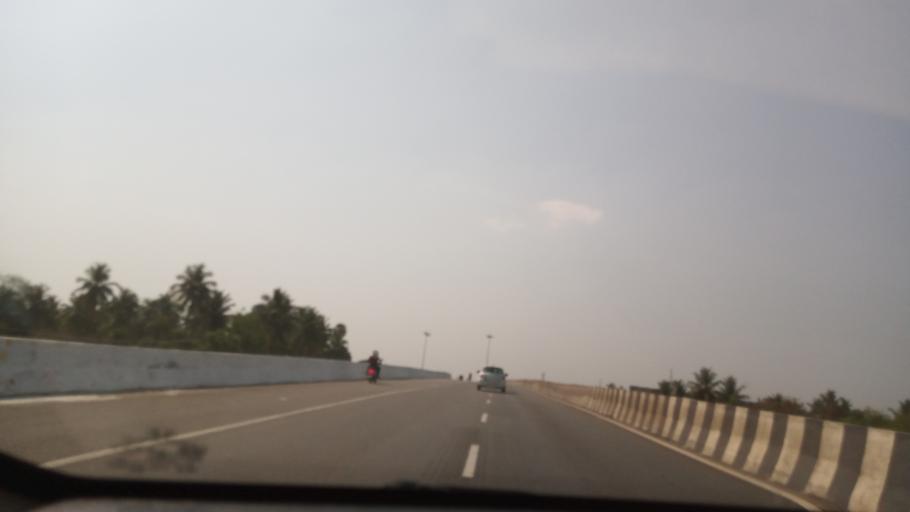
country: IN
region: Tamil Nadu
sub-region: Salem
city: Omalur
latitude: 11.7360
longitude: 78.0549
